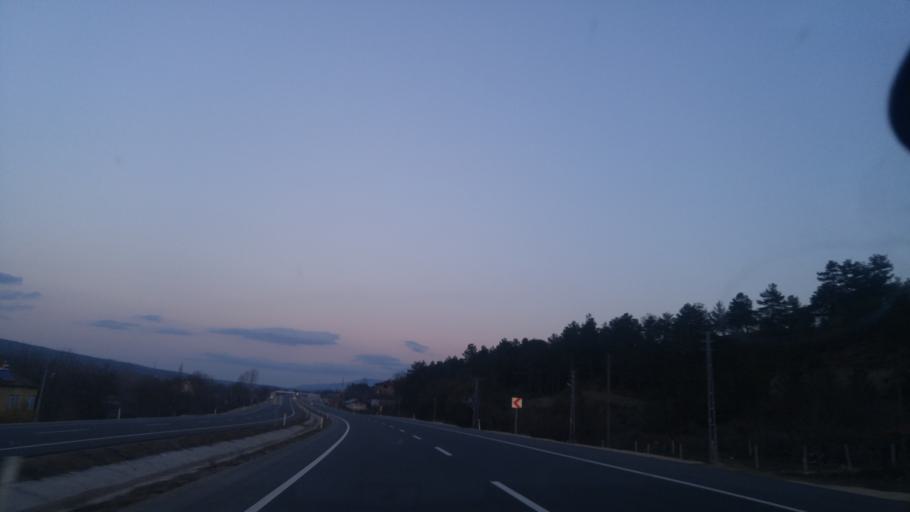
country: TR
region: Kastamonu
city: Igdir
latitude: 41.2290
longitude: 33.0880
